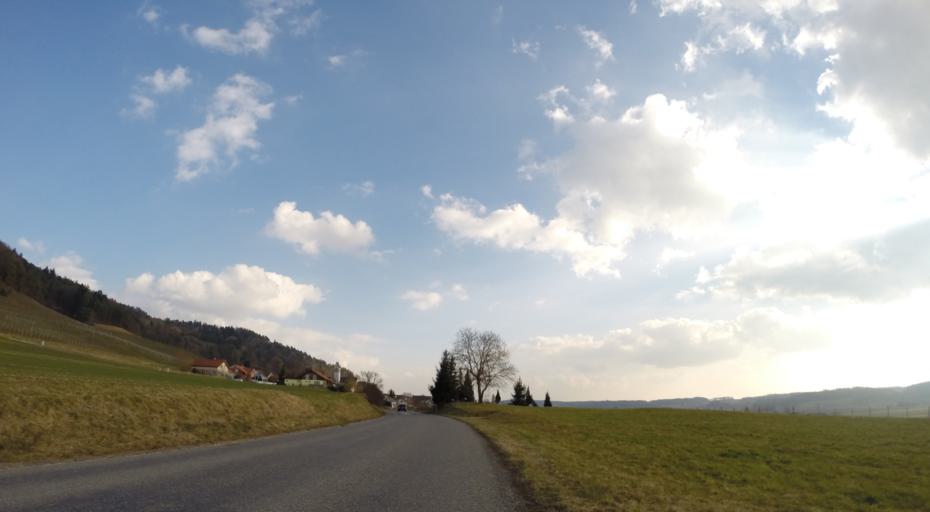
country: CH
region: Thurgau
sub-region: Frauenfeld District
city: Diessenhofen
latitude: 47.6454
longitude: 8.7881
